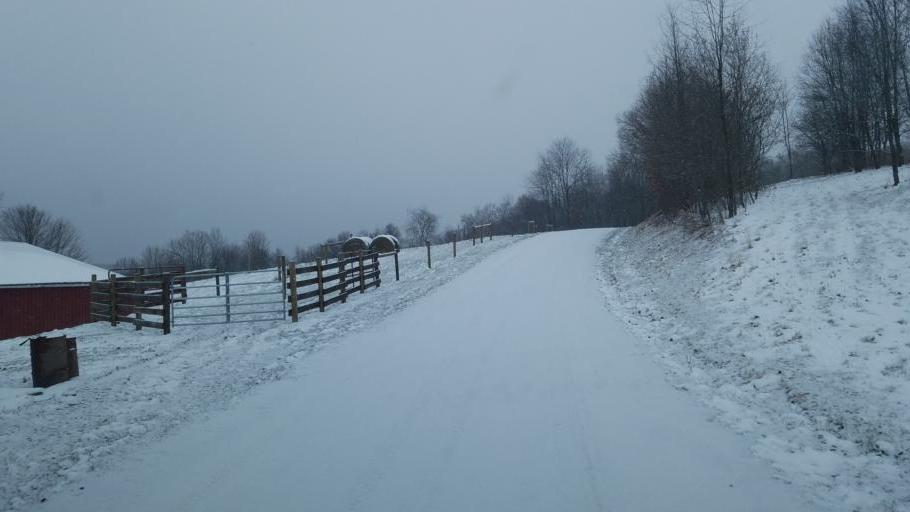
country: US
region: Pennsylvania
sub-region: Venango County
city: Sugarcreek
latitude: 41.4645
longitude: -79.9449
